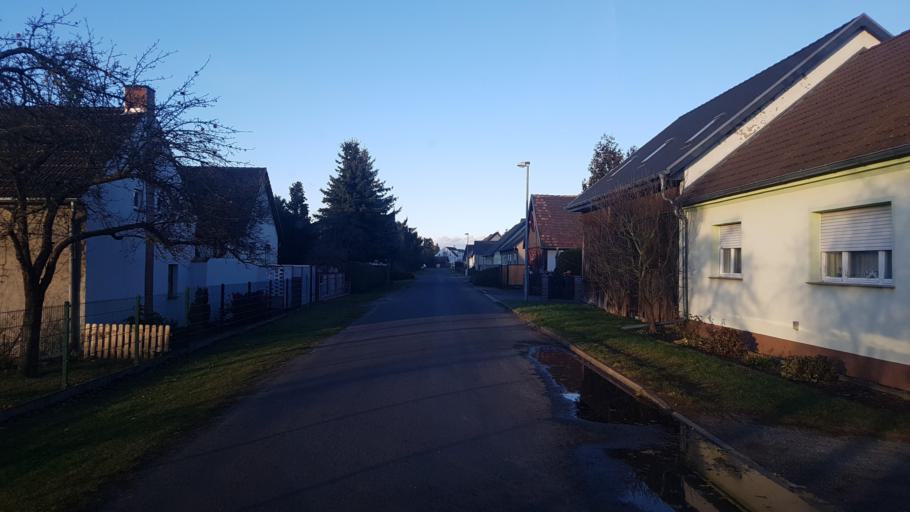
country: DE
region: Brandenburg
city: Drachhausen
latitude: 51.8877
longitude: 14.3195
